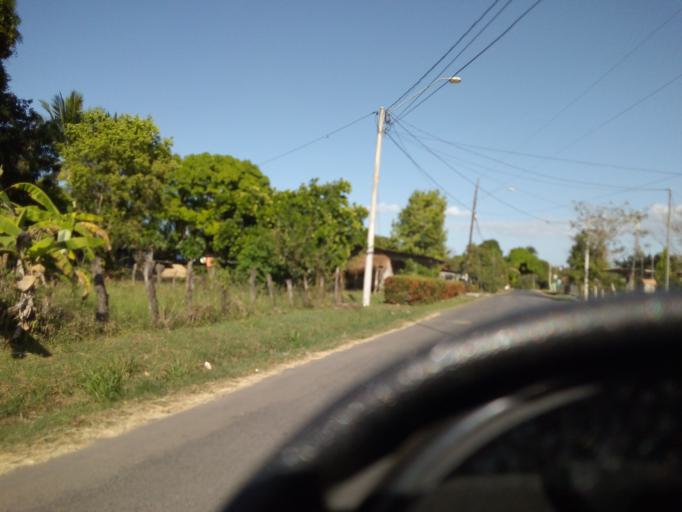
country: PA
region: Veraguas
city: Atalaya
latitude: 8.0380
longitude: -80.9232
